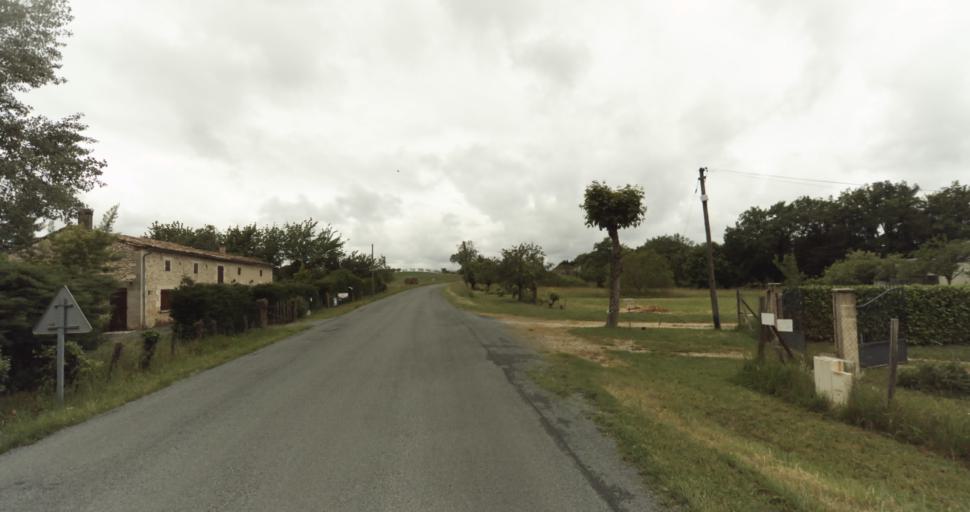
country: FR
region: Aquitaine
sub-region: Departement de la Dordogne
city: Beaumont-du-Perigord
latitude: 44.7030
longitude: 0.8366
